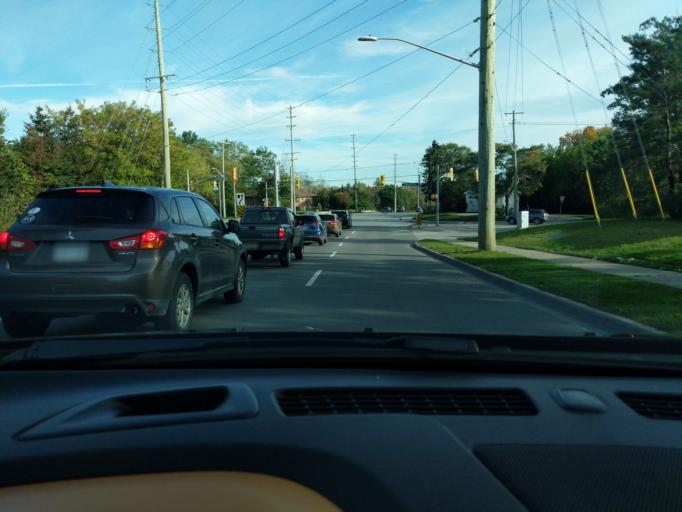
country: CA
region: Ontario
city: Barrie
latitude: 44.3817
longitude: -79.7253
